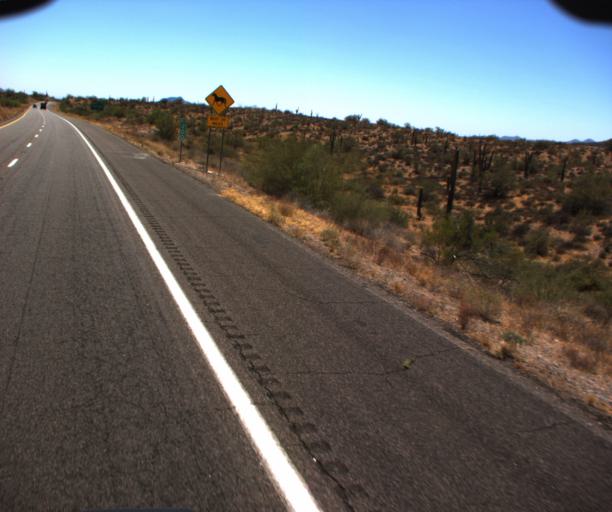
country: US
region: Arizona
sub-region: Maricopa County
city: Rio Verde
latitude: 33.6371
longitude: -111.5483
